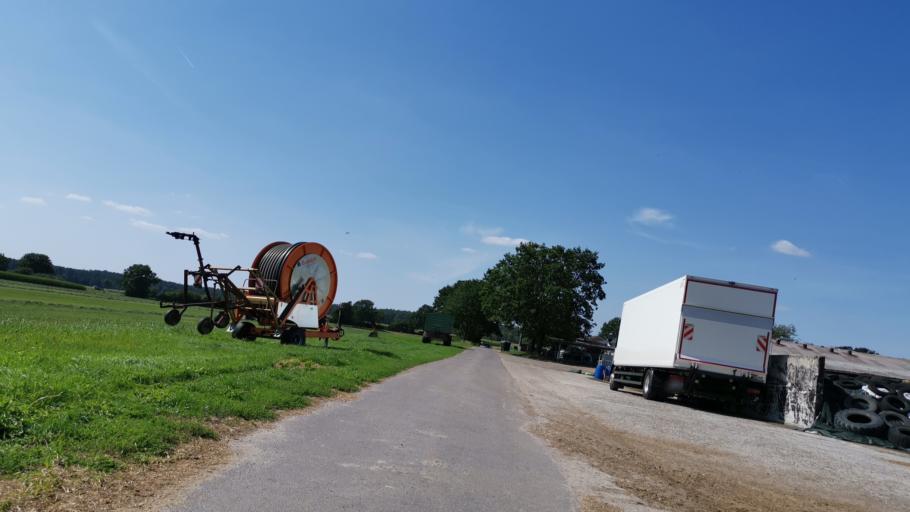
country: DE
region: Schleswig-Holstein
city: Gudow
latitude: 53.5737
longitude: 10.7678
